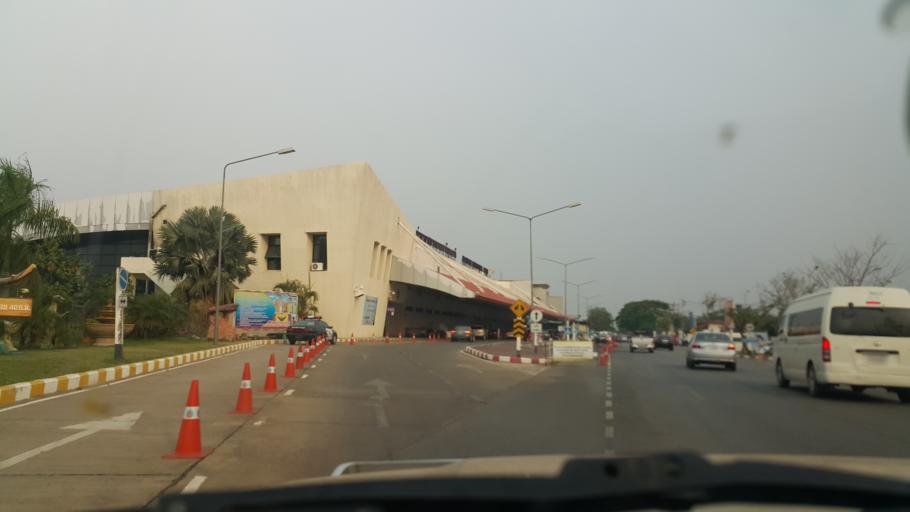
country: TH
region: Changwat Udon Thani
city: Udon Thani
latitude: 17.3872
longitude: 102.7741
